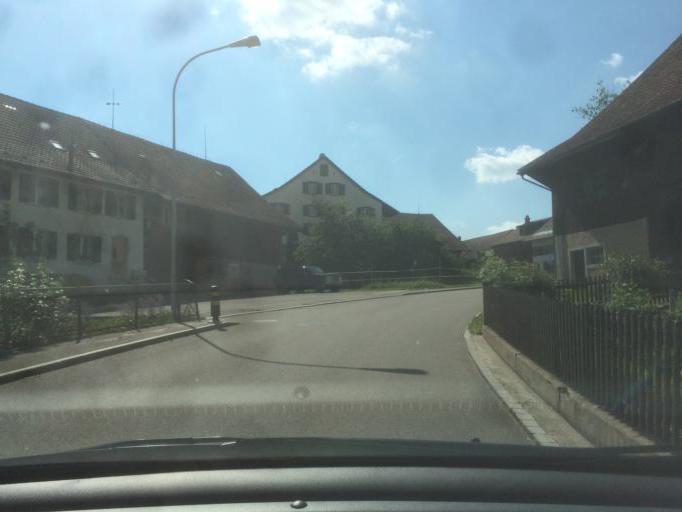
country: CH
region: Zurich
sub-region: Bezirk Hinwil
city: Wetzikon / Robenhausen
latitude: 47.3443
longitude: 8.7649
